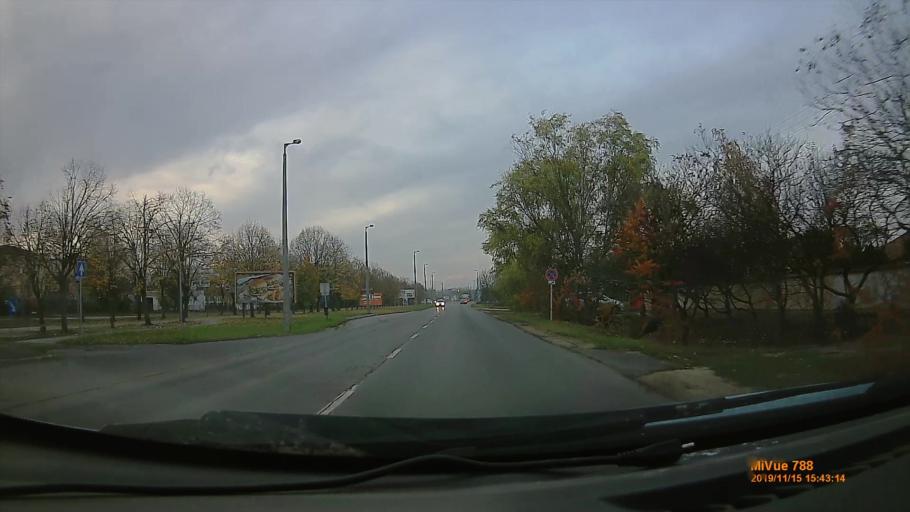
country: HU
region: Bekes
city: Bekescsaba
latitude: 46.6801
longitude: 21.1182
